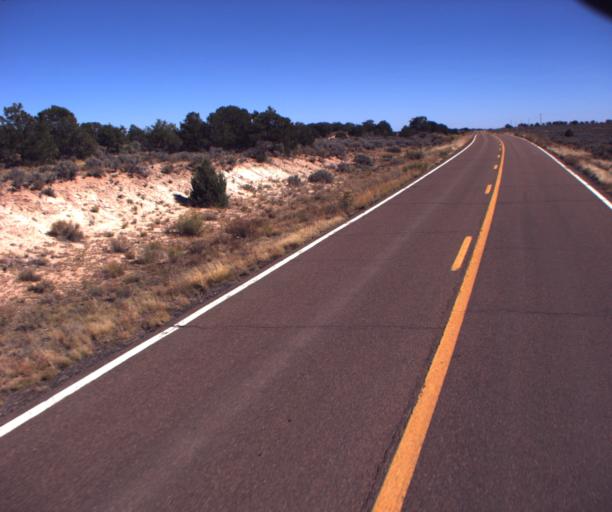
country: US
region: Arizona
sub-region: Apache County
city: Ganado
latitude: 35.7486
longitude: -109.9312
